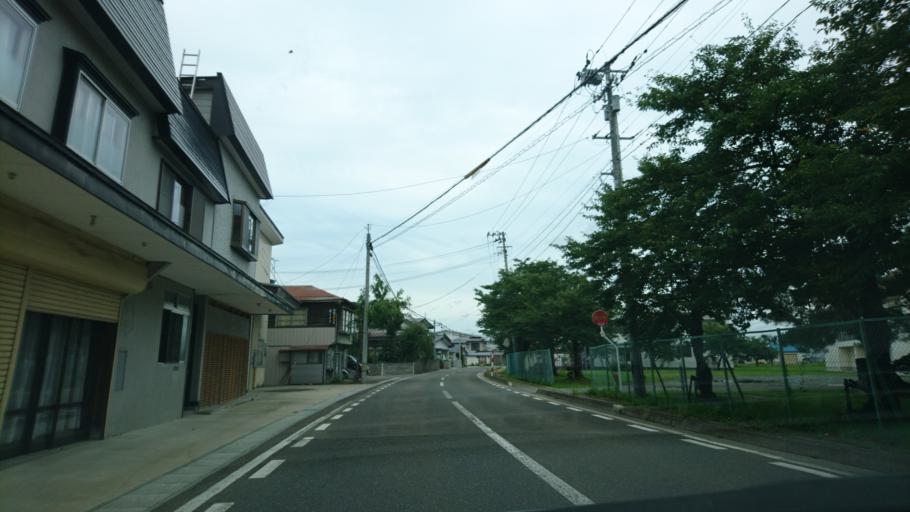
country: JP
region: Akita
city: Yuzawa
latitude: 39.1761
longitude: 140.5555
